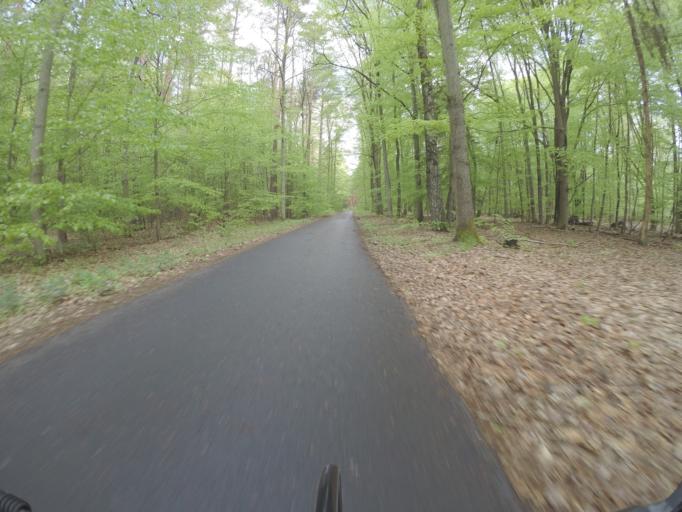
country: DE
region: Brandenburg
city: Marienwerder
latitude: 52.8654
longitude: 13.6146
